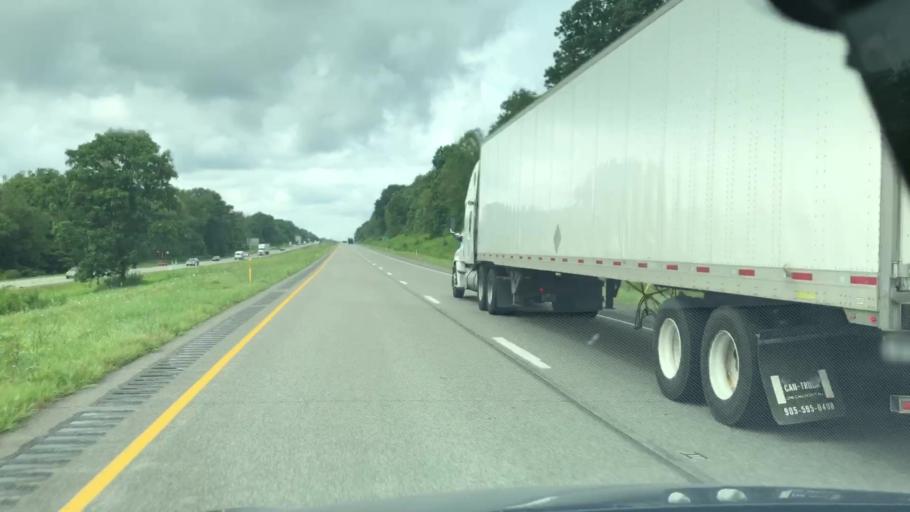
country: US
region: Pennsylvania
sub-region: Crawford County
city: Meadville
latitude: 41.6310
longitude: -80.1902
